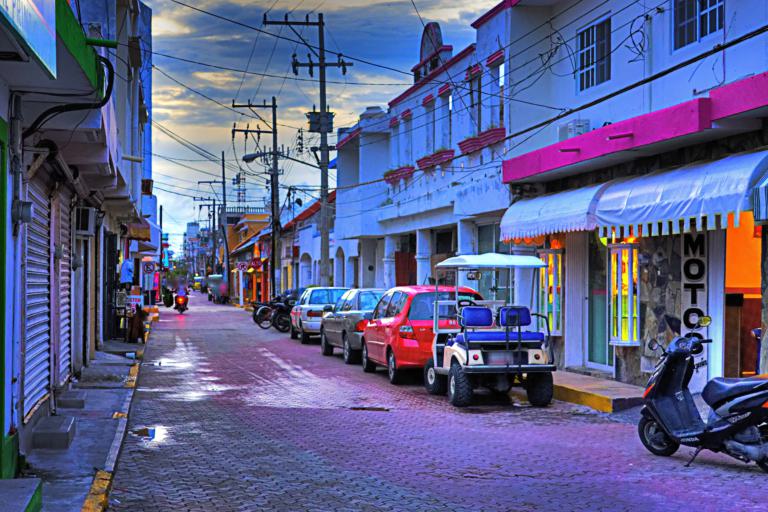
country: MX
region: Quintana Roo
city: Isla Mujeres
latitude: 21.2558
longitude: -86.7459
